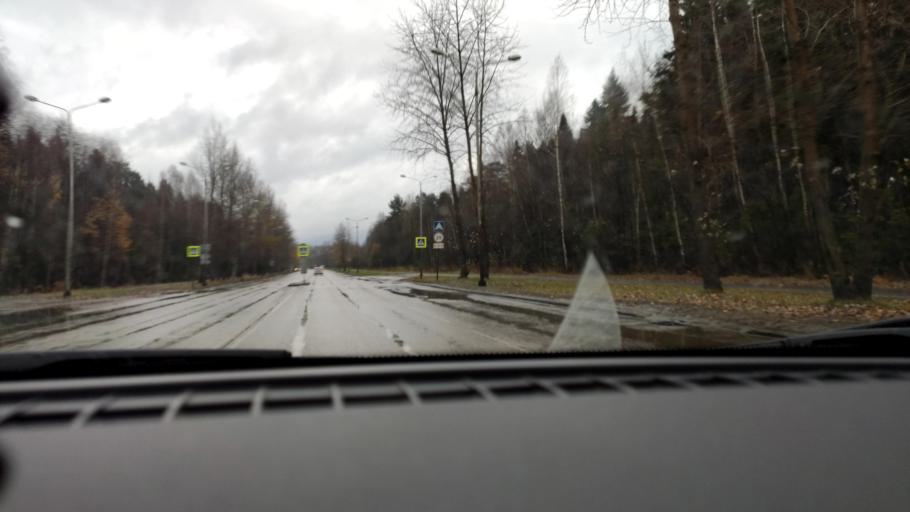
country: RU
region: Perm
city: Perm
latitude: 58.0857
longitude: 56.3782
